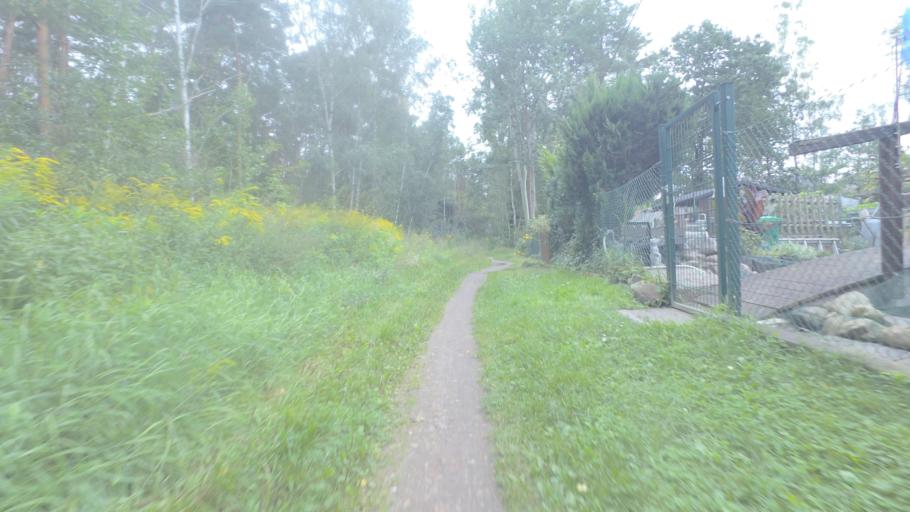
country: DE
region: Brandenburg
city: Ludwigsfelde
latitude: 52.2915
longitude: 13.2441
